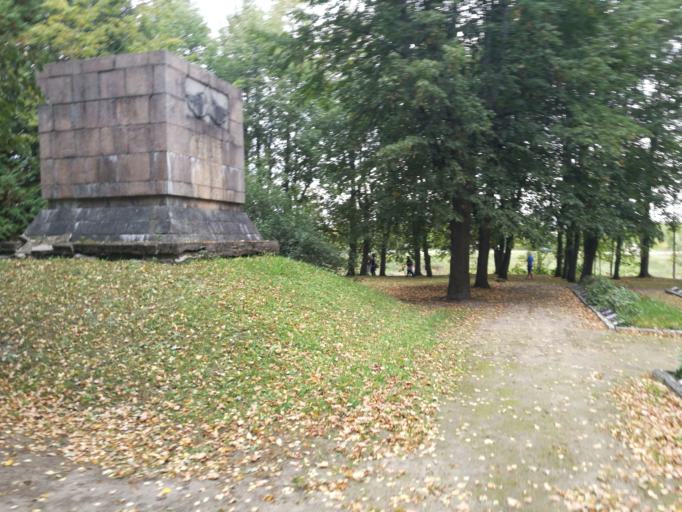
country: LV
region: Limbazu Rajons
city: Limbazi
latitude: 57.5161
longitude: 24.7178
